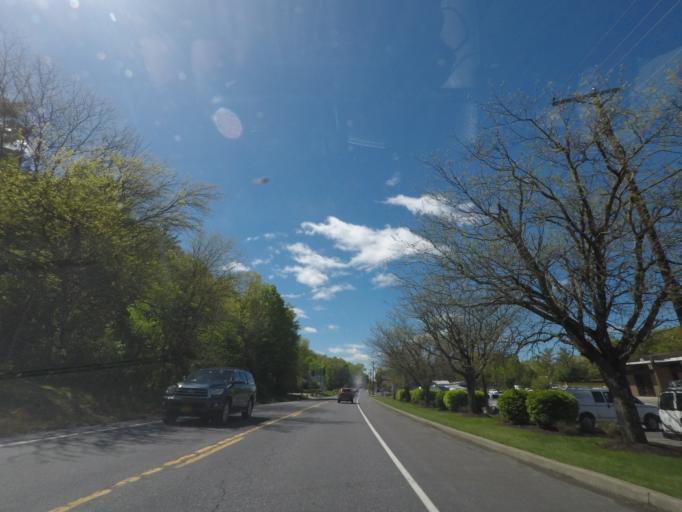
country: US
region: New York
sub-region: Ulster County
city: Lake Katrine
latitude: 41.9930
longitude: -73.9862
